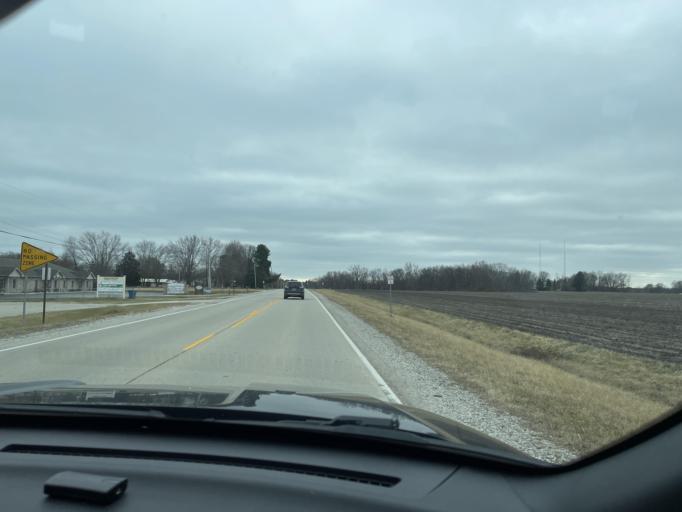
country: US
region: Illinois
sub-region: Sangamon County
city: Leland Grove
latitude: 39.8187
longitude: -89.7397
